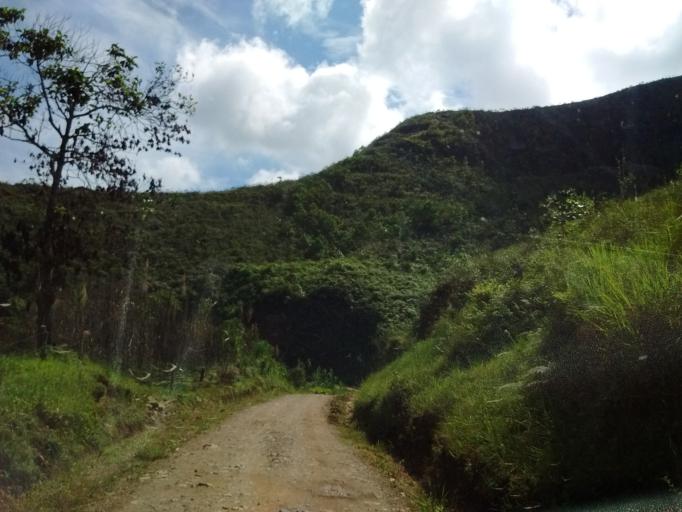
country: CO
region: Cauca
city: Morales
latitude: 2.6949
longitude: -76.7466
